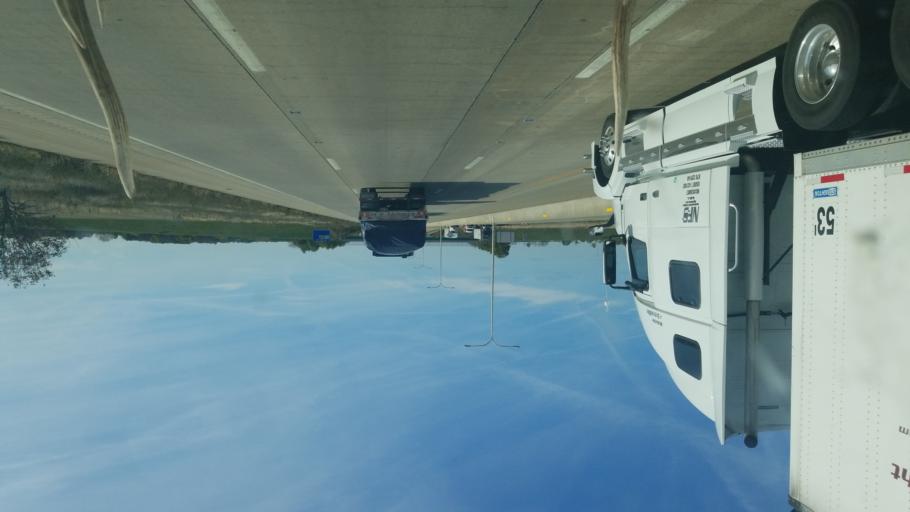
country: US
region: Illinois
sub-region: Effingham County
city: Effingham
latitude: 39.1430
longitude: -88.5461
